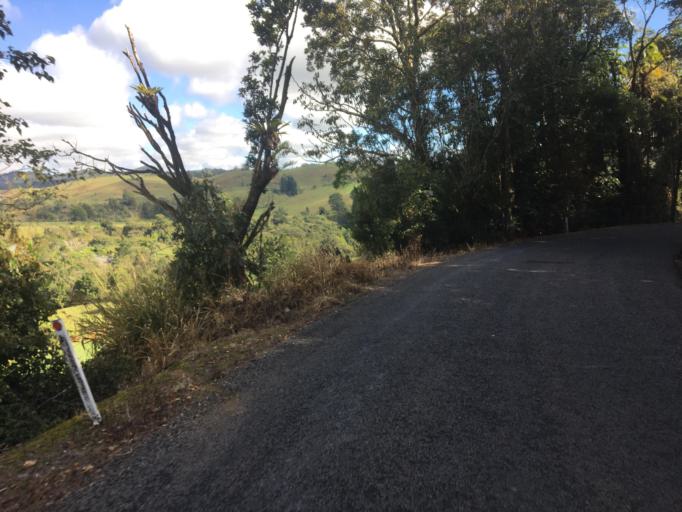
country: AU
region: Queensland
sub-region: Tablelands
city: Ravenshoe
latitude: -17.5351
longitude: 145.6074
